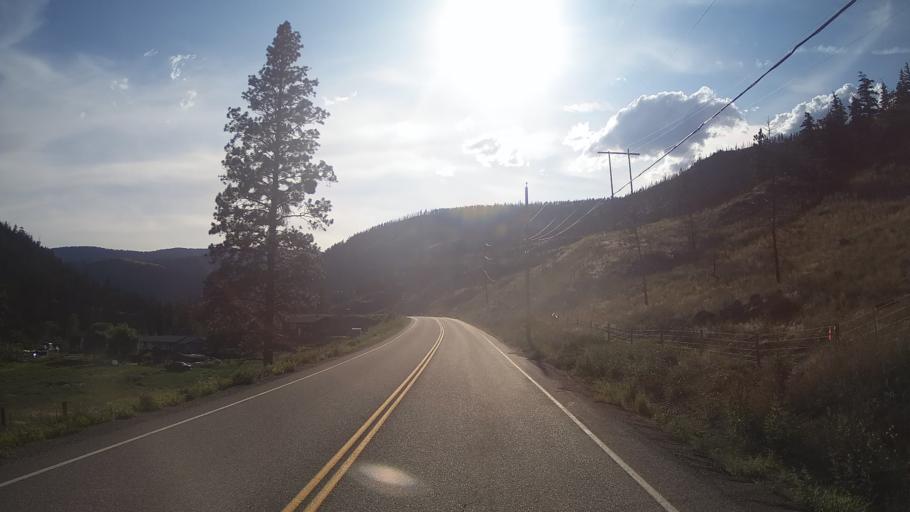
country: CA
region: British Columbia
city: Cache Creek
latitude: 50.8848
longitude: -121.4887
